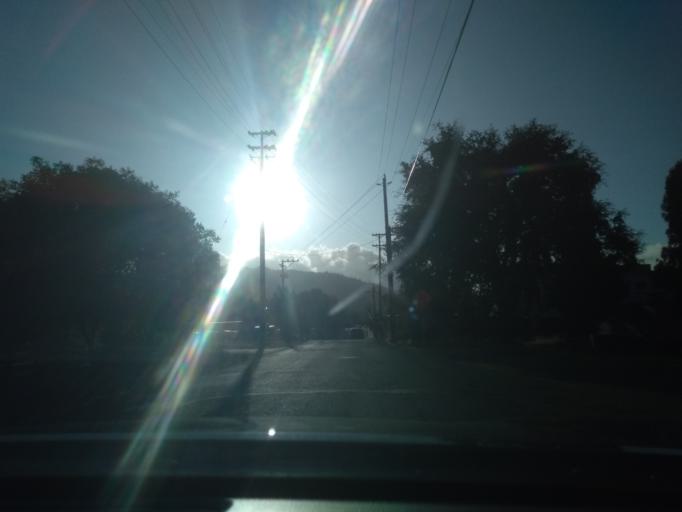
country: US
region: California
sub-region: Mendocino County
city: Ukiah
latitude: 39.1593
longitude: -123.2050
